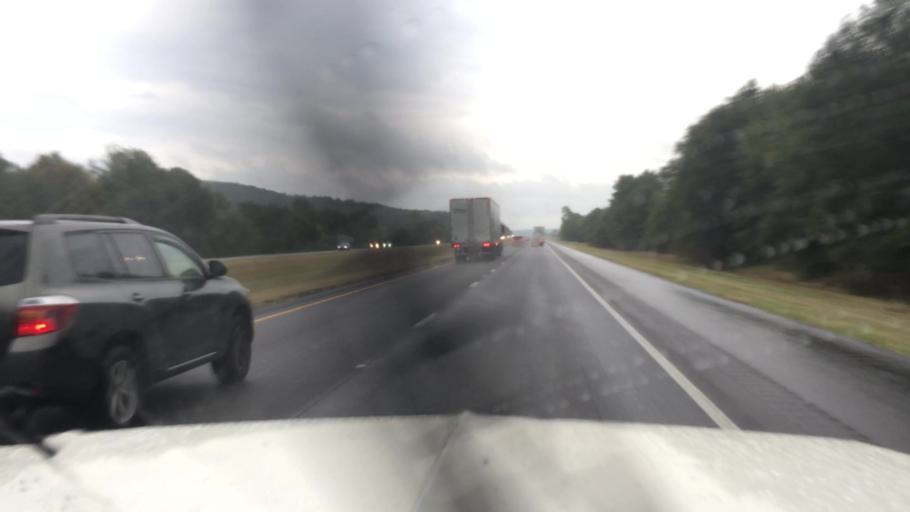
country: US
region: Alabama
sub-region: Morgan County
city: Falkville
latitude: 34.3973
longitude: -86.8969
